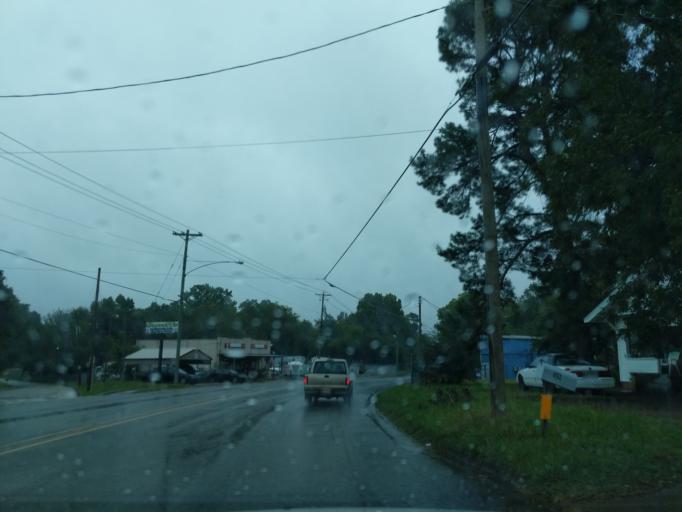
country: US
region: Texas
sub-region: Panola County
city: Carthage
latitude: 32.1579
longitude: -94.3318
